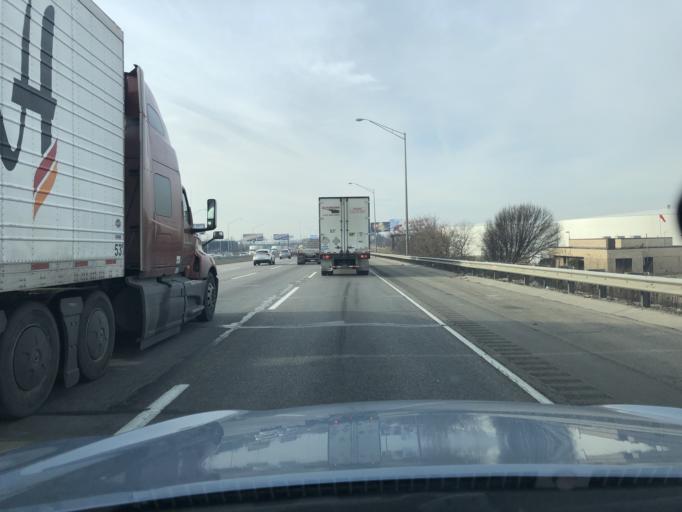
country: US
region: Illinois
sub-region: Cook County
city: Northlake
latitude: 41.9398
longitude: -87.8967
